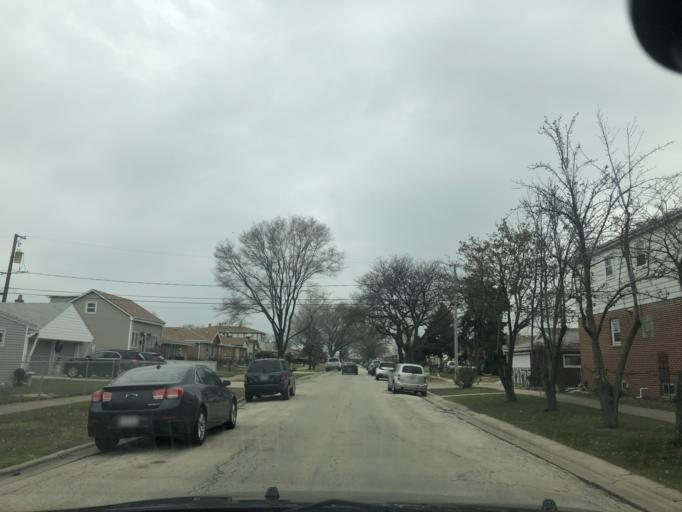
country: US
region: Illinois
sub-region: Cook County
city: Schiller Park
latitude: 41.9694
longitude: -87.8687
